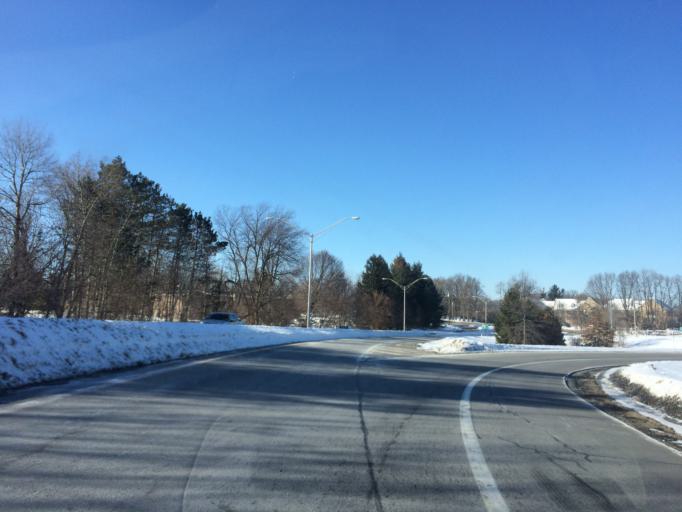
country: US
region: New York
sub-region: Monroe County
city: Pittsford
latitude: 43.1101
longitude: -77.5087
